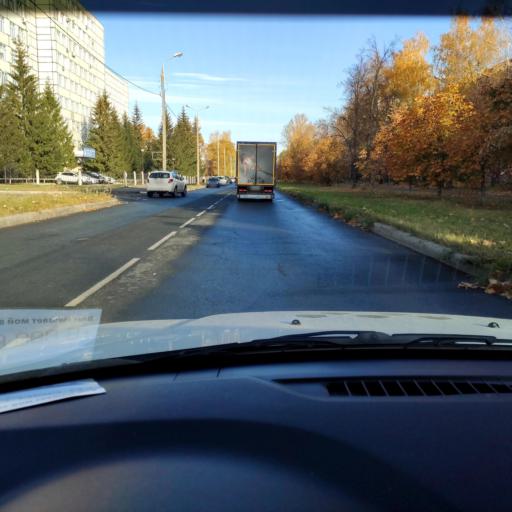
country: RU
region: Samara
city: Tol'yatti
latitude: 53.4992
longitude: 49.4019
